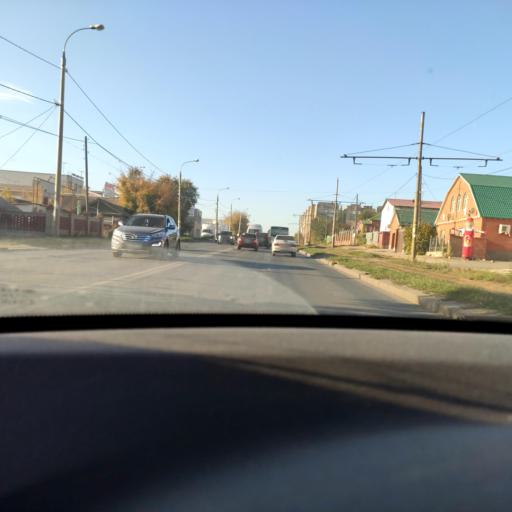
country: RU
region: Samara
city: Samara
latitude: 53.1937
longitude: 50.2157
